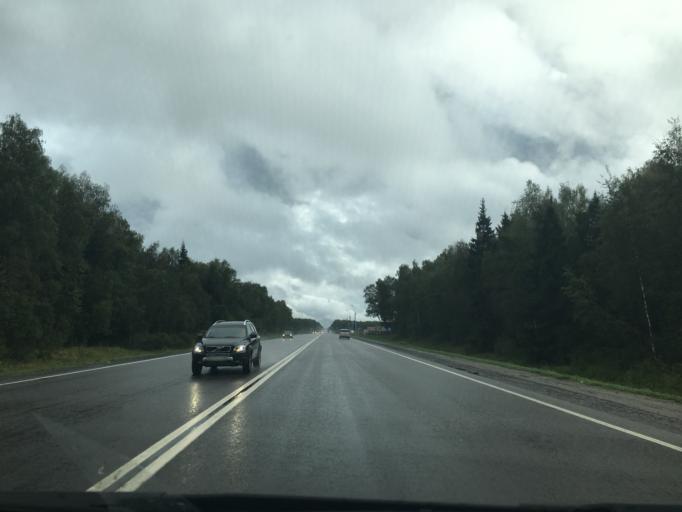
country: RU
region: Kaluga
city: Balabanovo
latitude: 55.1586
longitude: 36.6660
